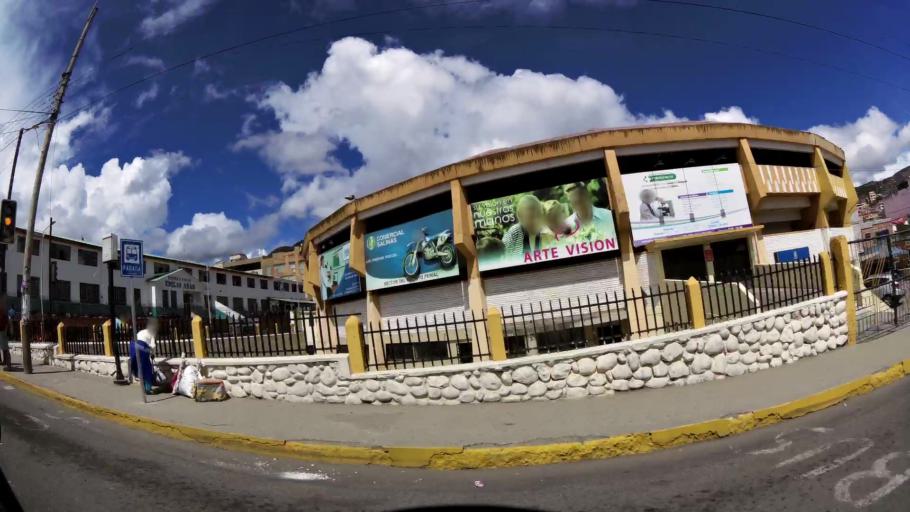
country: EC
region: Canar
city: Azogues
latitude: -2.7411
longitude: -78.8488
